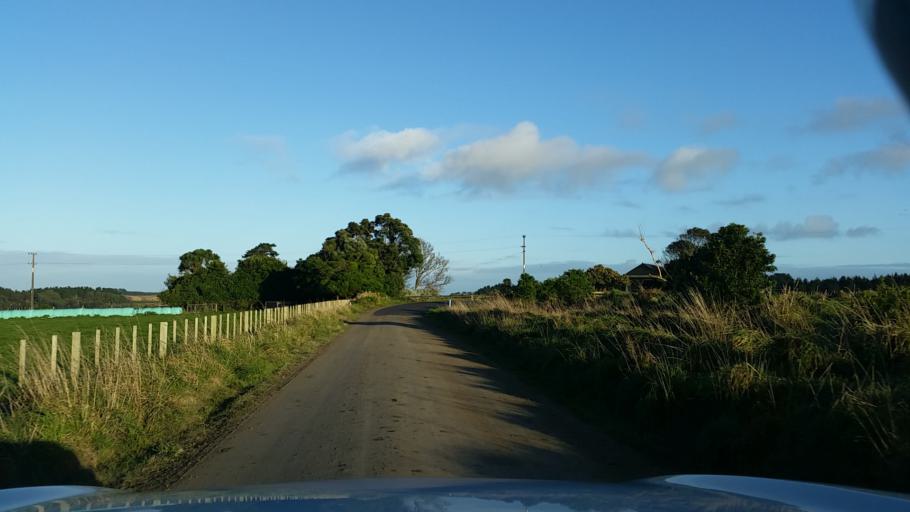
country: NZ
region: Manawatu-Wanganui
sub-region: Wanganui District
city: Wanganui
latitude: -39.8204
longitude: 174.7951
